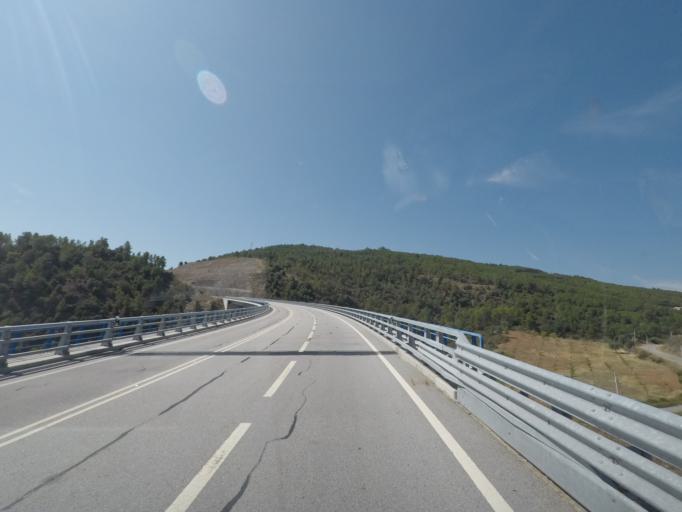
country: PT
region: Braganca
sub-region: Braganca Municipality
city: Vila Flor
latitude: 41.3164
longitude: -7.1223
